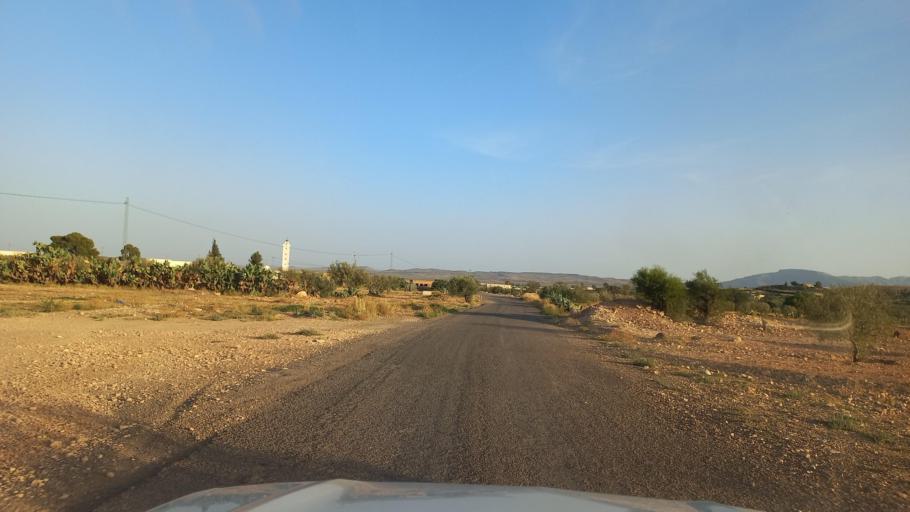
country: TN
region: Al Qasrayn
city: Kasserine
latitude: 35.2669
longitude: 8.9325
